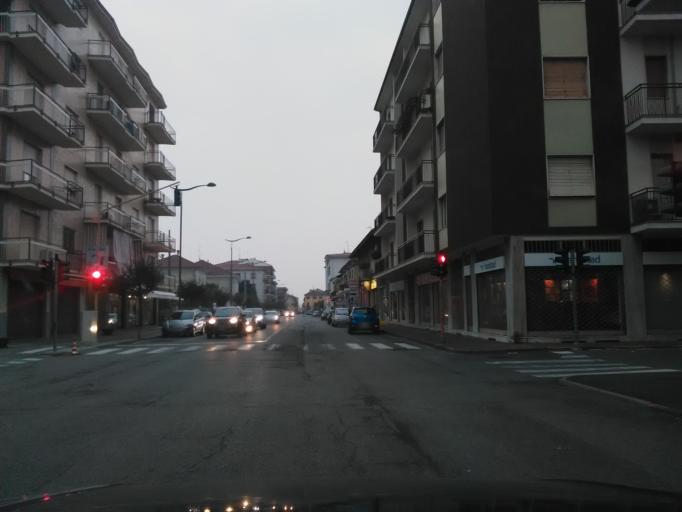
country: IT
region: Piedmont
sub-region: Provincia di Vercelli
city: Santhia
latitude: 45.3678
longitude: 8.1675
